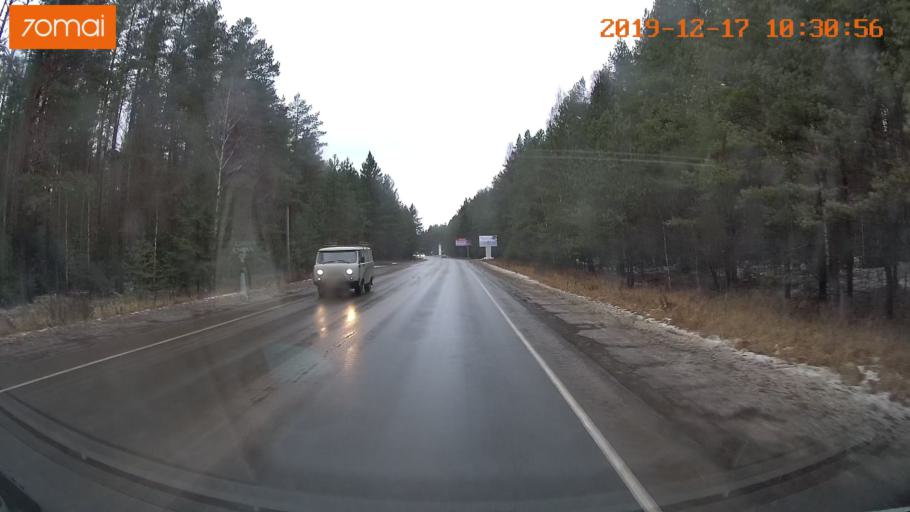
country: RU
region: Vladimir
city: Gus'-Khrustal'nyy
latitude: 55.6391
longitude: 40.7027
